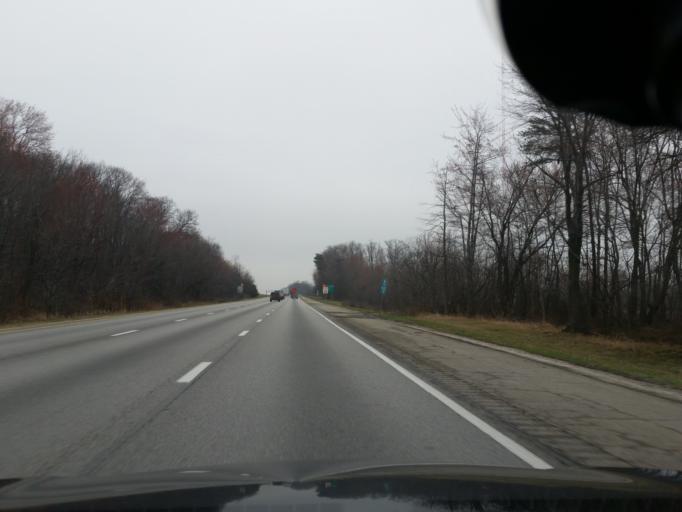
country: US
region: Pennsylvania
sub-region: Cumberland County
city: Enola
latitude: 40.3056
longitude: -76.9549
